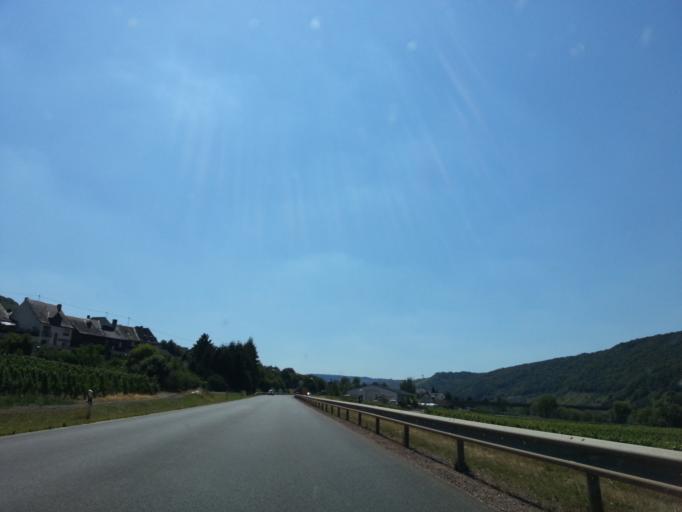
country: DE
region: Rheinland-Pfalz
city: Neumagen-Dhron
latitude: 49.8638
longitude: 6.8989
